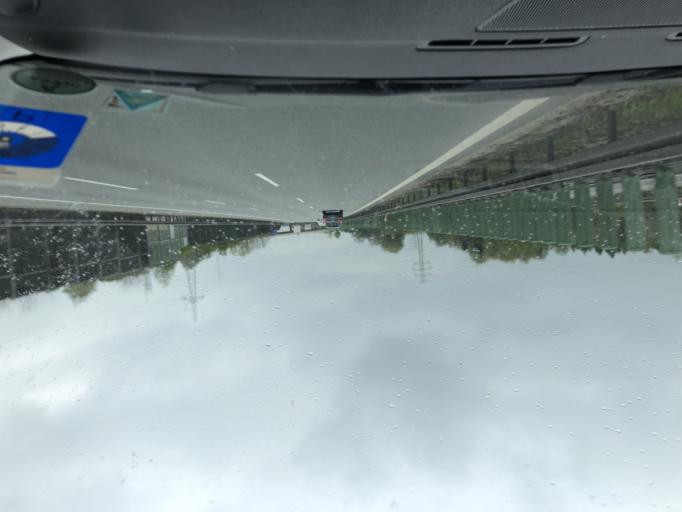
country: PL
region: Lesser Poland Voivodeship
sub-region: Powiat krakowski
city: Ochojno
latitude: 50.0015
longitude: 19.9988
